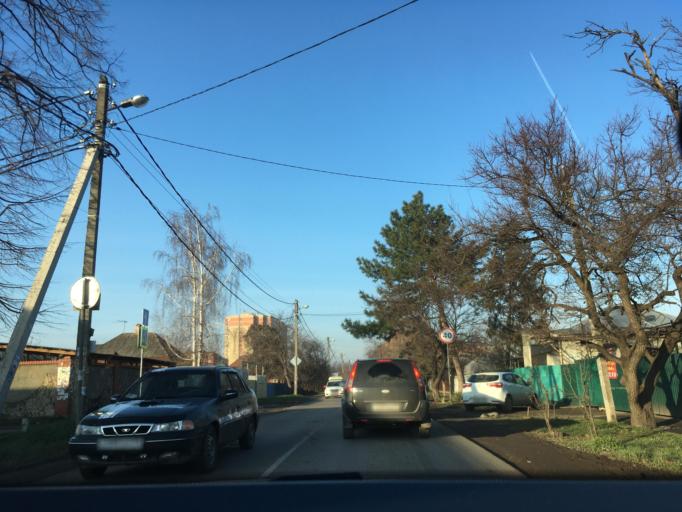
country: RU
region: Krasnodarskiy
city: Krasnodar
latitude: 45.0816
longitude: 39.0205
